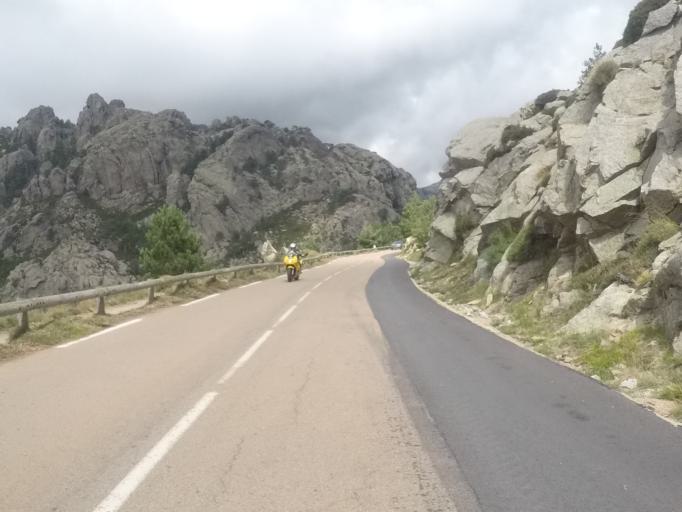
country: FR
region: Corsica
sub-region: Departement de la Corse-du-Sud
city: Zonza
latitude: 41.7940
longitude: 9.2224
